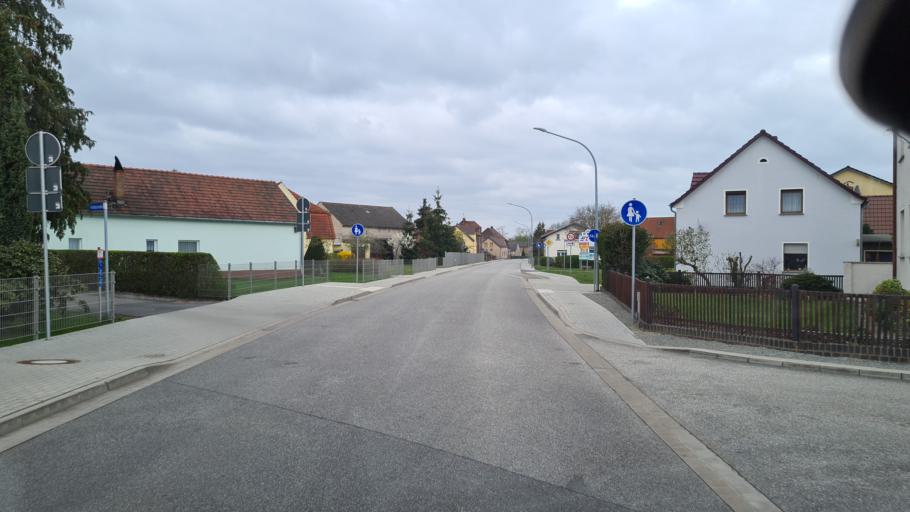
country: DE
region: Brandenburg
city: Hohenbocka
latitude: 51.4550
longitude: 14.0333
